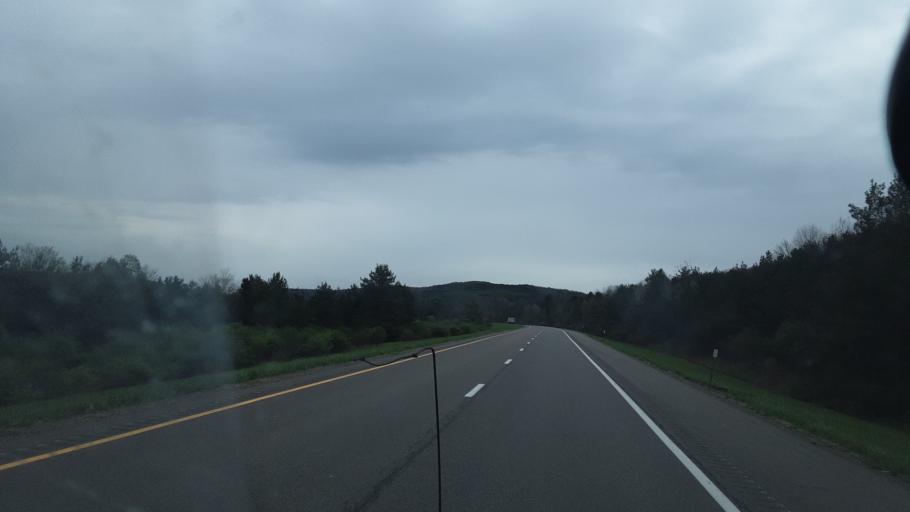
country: US
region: New York
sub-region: Allegany County
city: Belmont
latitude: 42.2945
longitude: -77.9919
